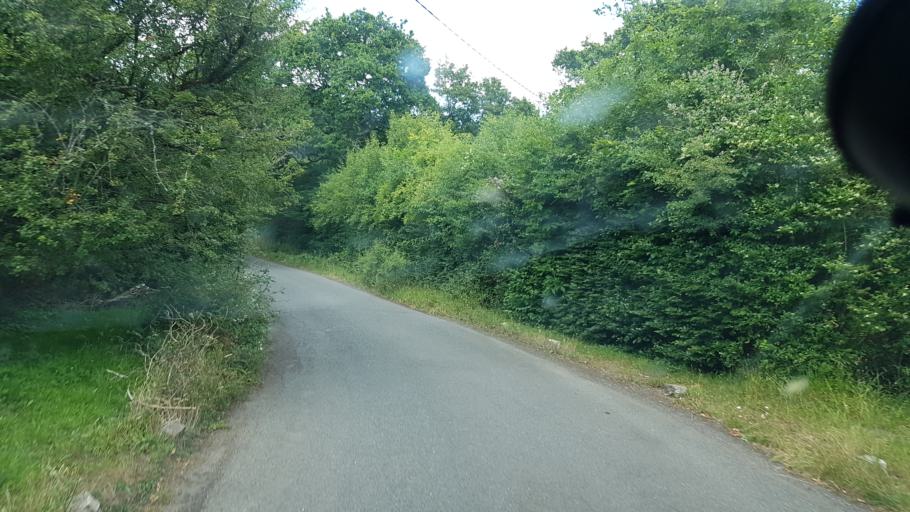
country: GB
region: England
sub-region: West Sussex
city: Billingshurst
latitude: 51.0280
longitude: -0.4312
